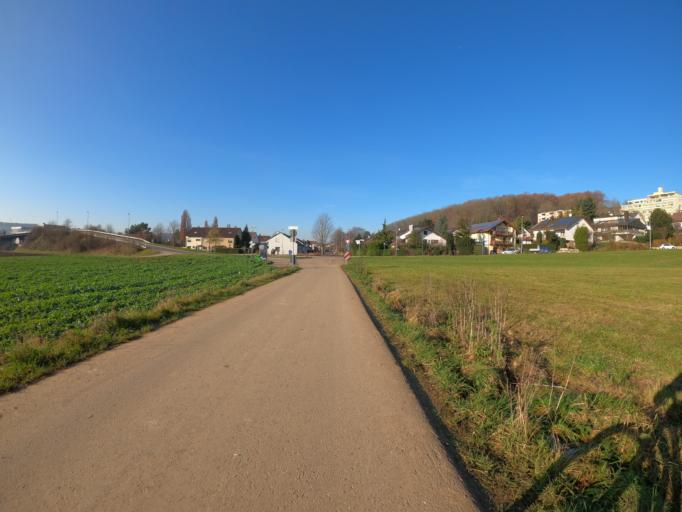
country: DE
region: Baden-Wuerttemberg
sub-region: Regierungsbezirk Stuttgart
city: Uhingen
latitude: 48.7094
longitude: 9.5938
